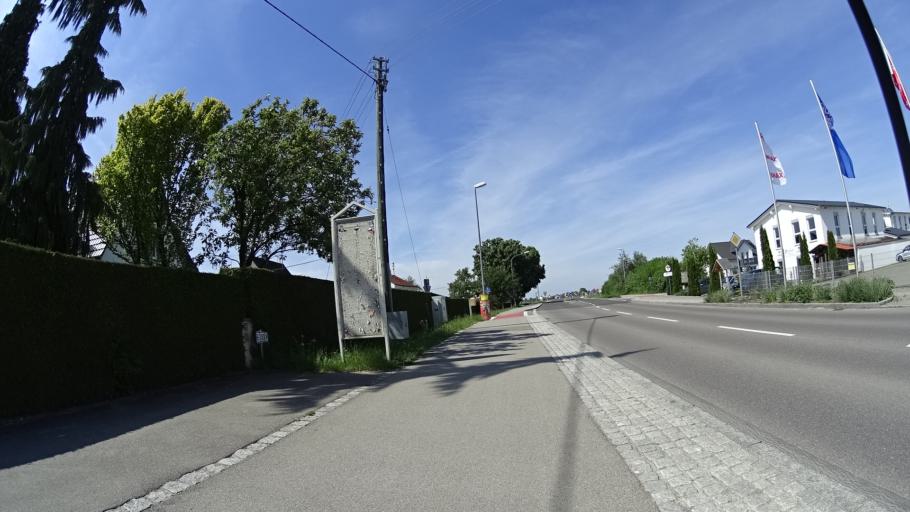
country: DE
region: Bavaria
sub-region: Swabia
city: Weissenhorn
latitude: 48.3161
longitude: 10.1555
